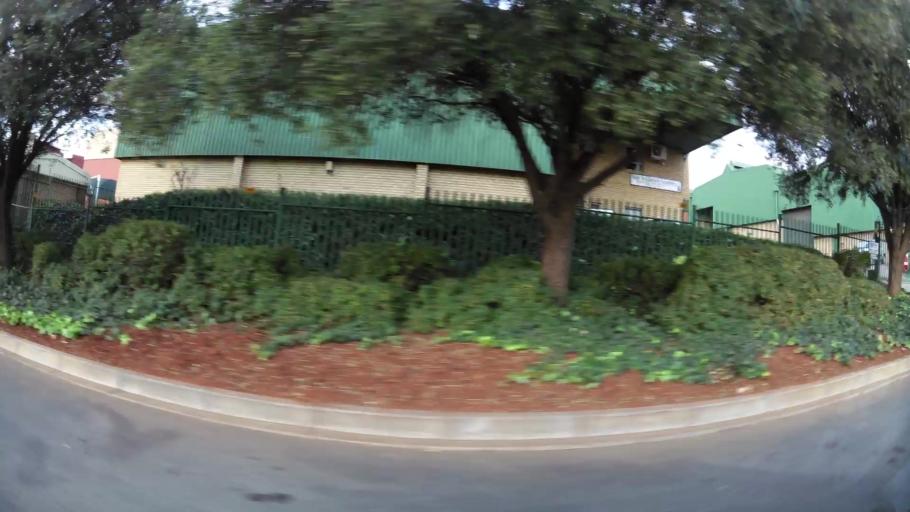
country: ZA
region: Gauteng
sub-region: City of Johannesburg Metropolitan Municipality
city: Modderfontein
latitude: -26.1515
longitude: 28.1818
